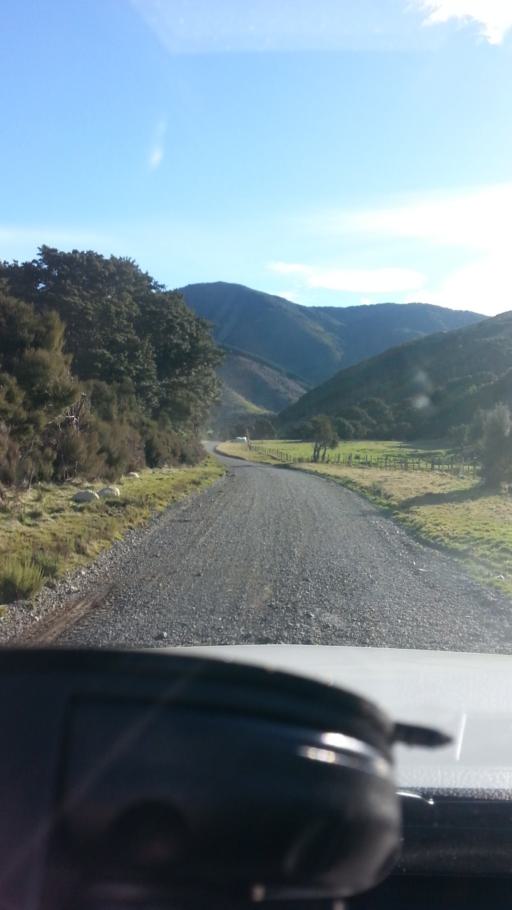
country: NZ
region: Wellington
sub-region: Masterton District
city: Masterton
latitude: -40.8822
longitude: 175.5067
